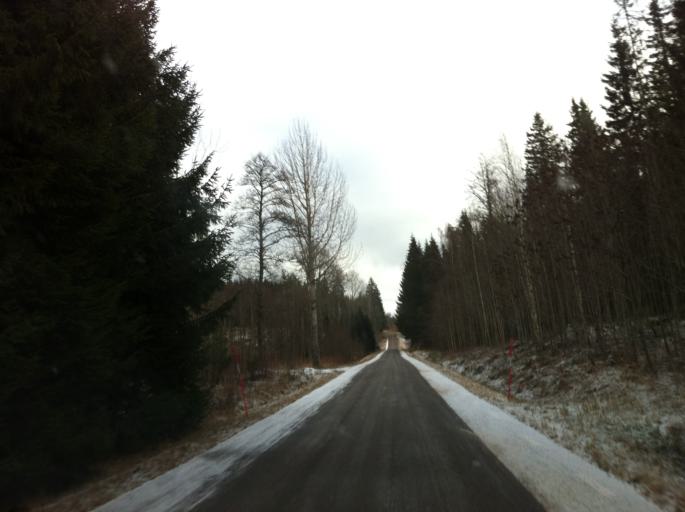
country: SE
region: Joenkoeping
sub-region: Eksjo Kommun
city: Mariannelund
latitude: 57.6112
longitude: 15.6895
